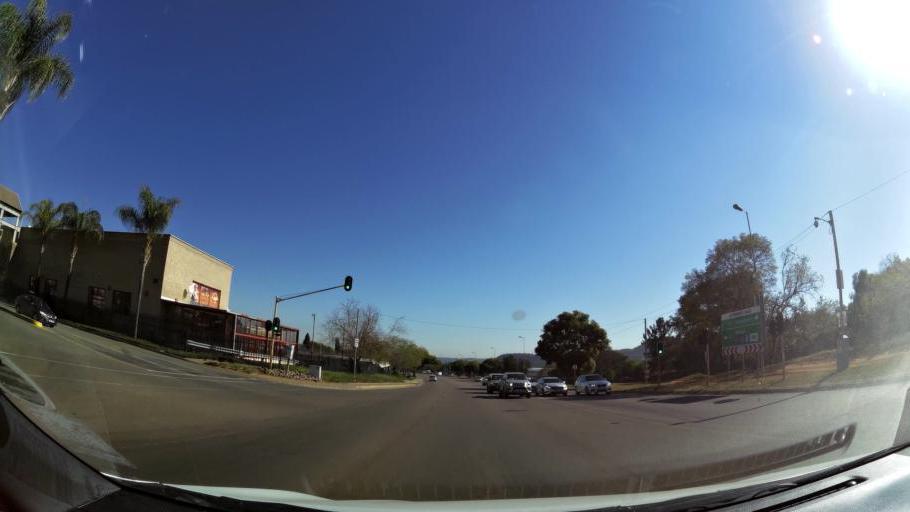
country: ZA
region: Gauteng
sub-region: City of Tshwane Metropolitan Municipality
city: Pretoria
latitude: -25.7873
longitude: 28.3078
